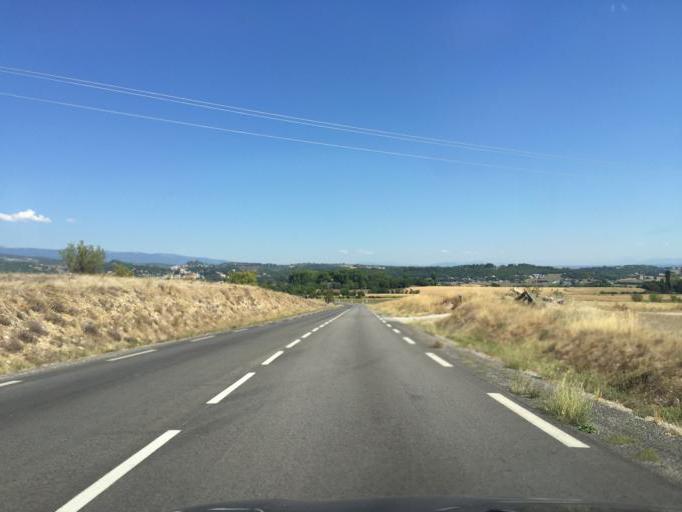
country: FR
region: Provence-Alpes-Cote d'Azur
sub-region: Departement des Alpes-de-Haute-Provence
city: Mane
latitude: 43.9137
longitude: 5.7526
